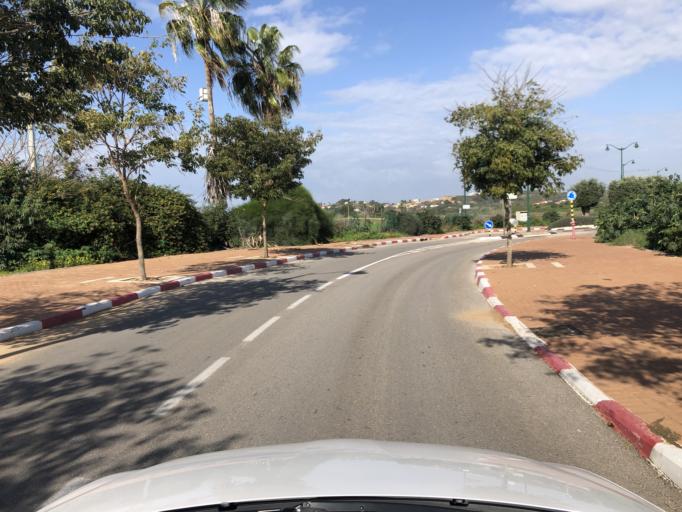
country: IL
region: Central District
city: Ness Ziona
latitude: 31.9102
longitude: 34.7831
